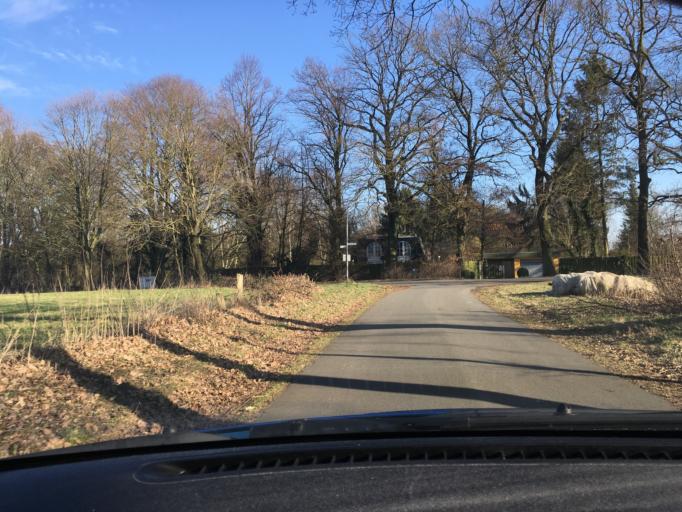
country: DE
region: Lower Saxony
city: Seevetal
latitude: 53.4005
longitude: 9.9856
